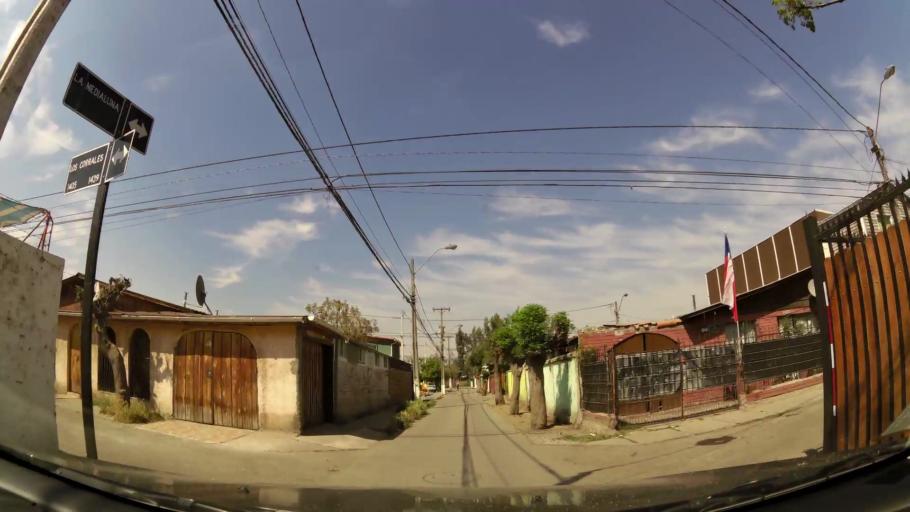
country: CL
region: Santiago Metropolitan
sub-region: Provincia de Santiago
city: La Pintana
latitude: -33.5656
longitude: -70.6001
